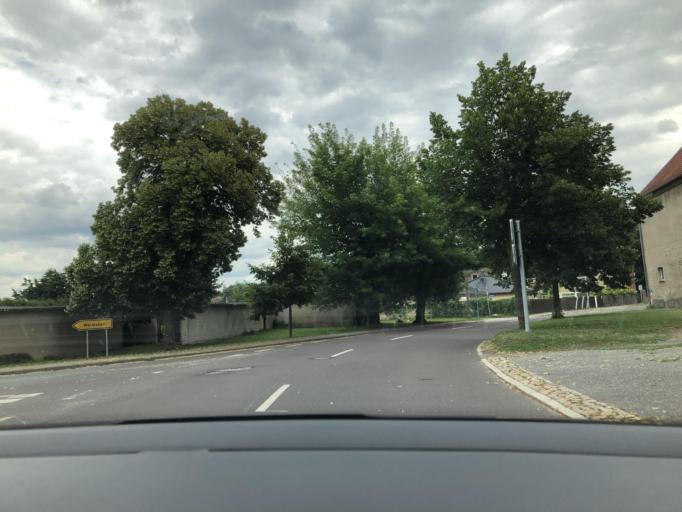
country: DE
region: Saxony-Anhalt
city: Biere
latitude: 51.9750
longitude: 11.6537
